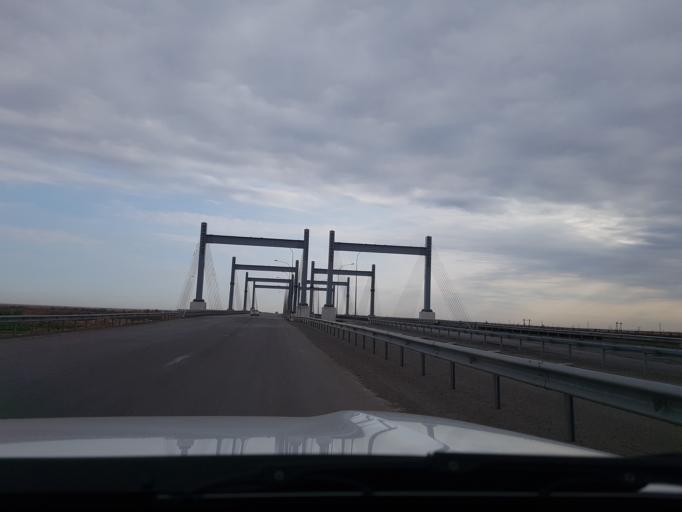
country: TM
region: Ahal
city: Tejen
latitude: 37.2312
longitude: 60.1491
